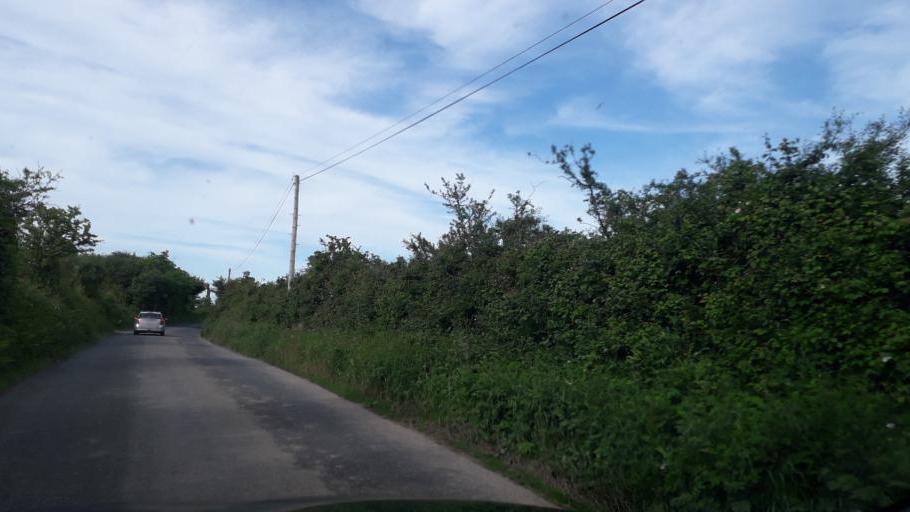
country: IE
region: Leinster
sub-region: Loch Garman
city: Courtown
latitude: 52.5268
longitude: -6.2694
